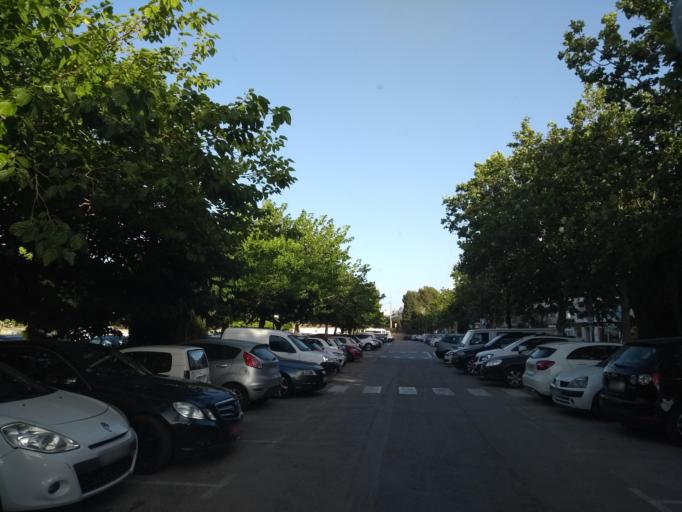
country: ES
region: Balearic Islands
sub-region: Illes Balears
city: Port d'Alcudia
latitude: 39.8432
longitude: 3.1343
